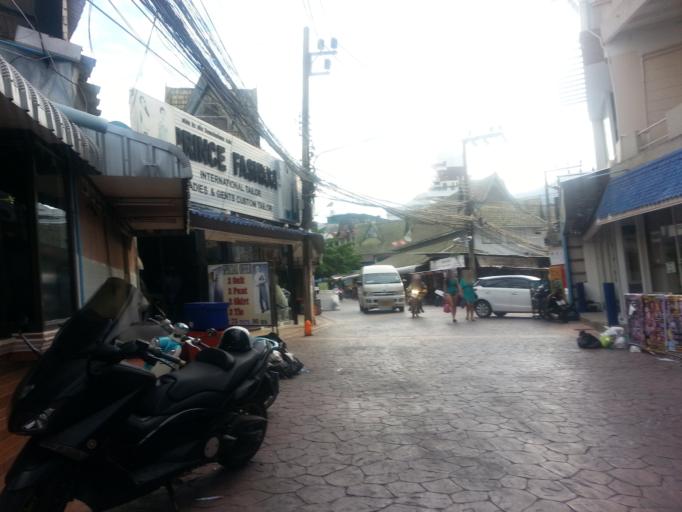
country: TH
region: Phuket
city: Patong
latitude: 7.8892
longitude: 98.2944
